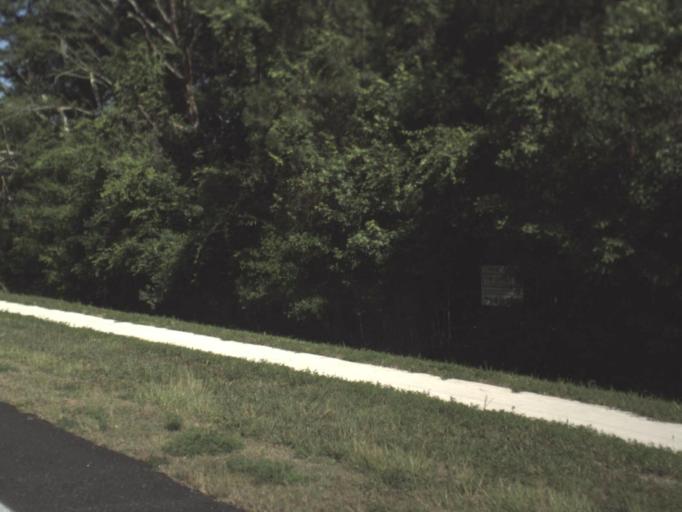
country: US
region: Florida
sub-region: Saint Johns County
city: Saint Augustine
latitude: 29.9140
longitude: -81.3886
